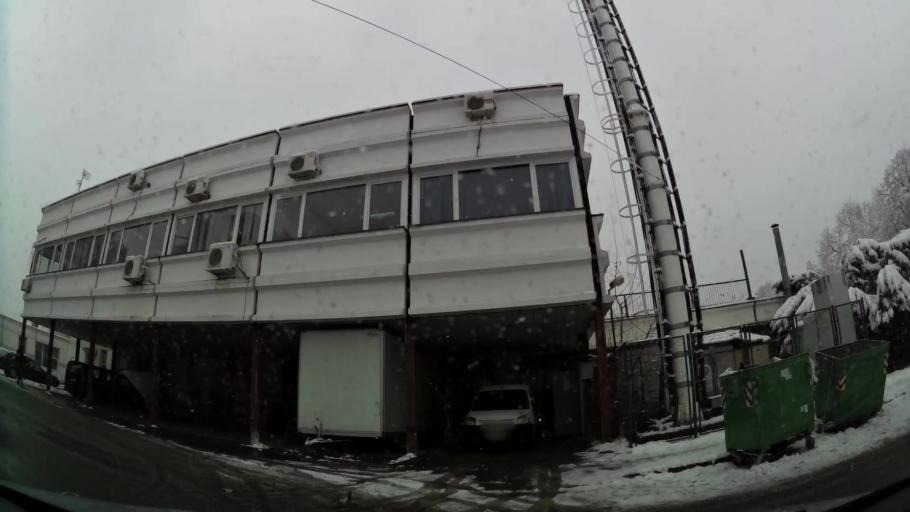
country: RS
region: Central Serbia
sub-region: Belgrade
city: Novi Beograd
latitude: 44.8011
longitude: 20.3942
